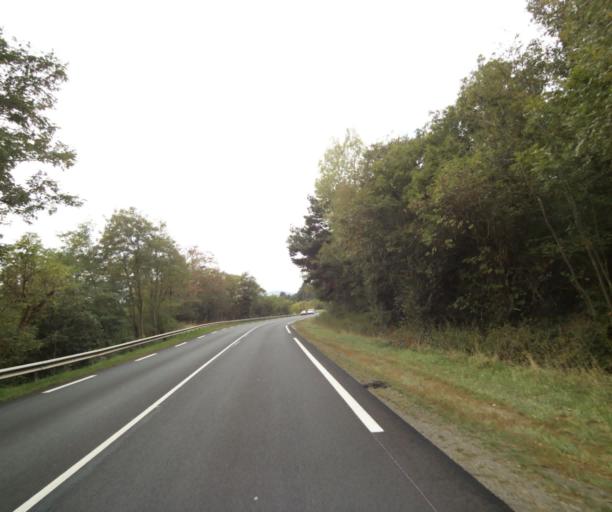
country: FR
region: Auvergne
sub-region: Departement du Puy-de-Dome
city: Saint-Genes-Champanelle
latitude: 45.7064
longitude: 3.0332
